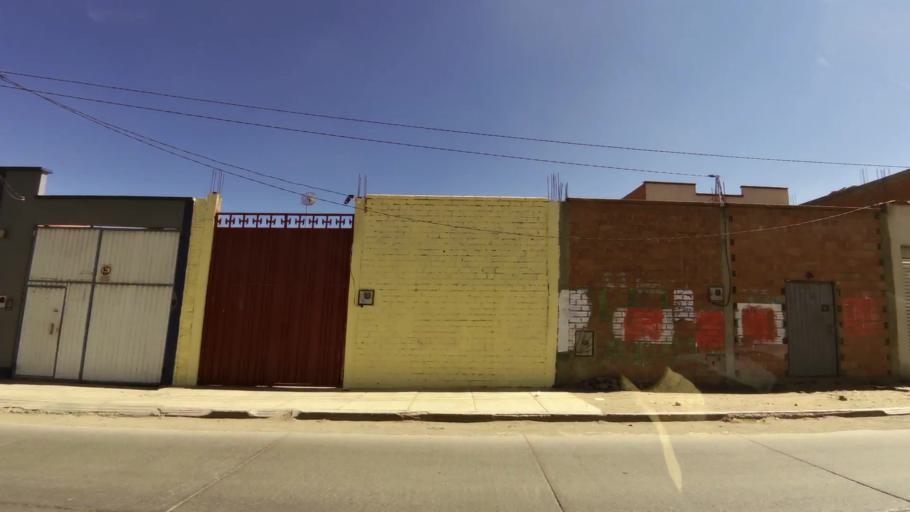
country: BO
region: La Paz
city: La Paz
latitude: -16.4976
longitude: -68.2069
